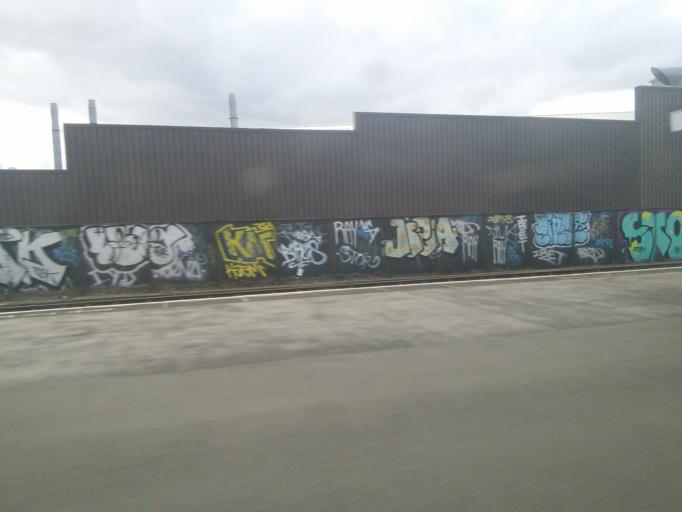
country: GB
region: England
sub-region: City and Borough of Birmingham
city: Birmingham
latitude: 52.4720
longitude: -1.8777
